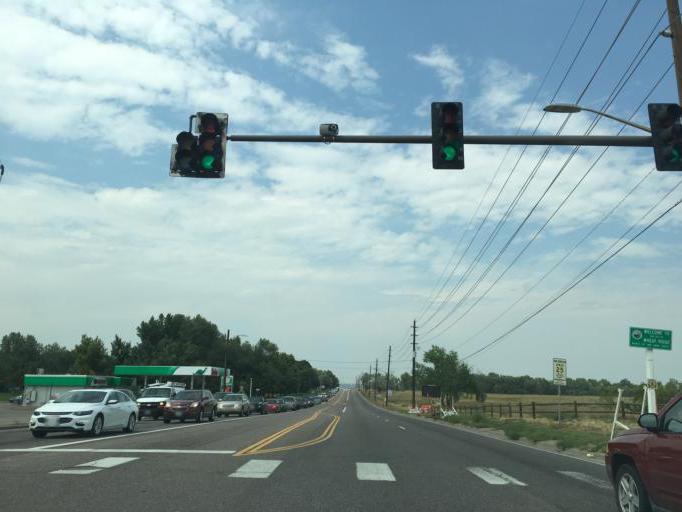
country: US
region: Colorado
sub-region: Jefferson County
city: Wheat Ridge
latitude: 39.7546
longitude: -105.1096
